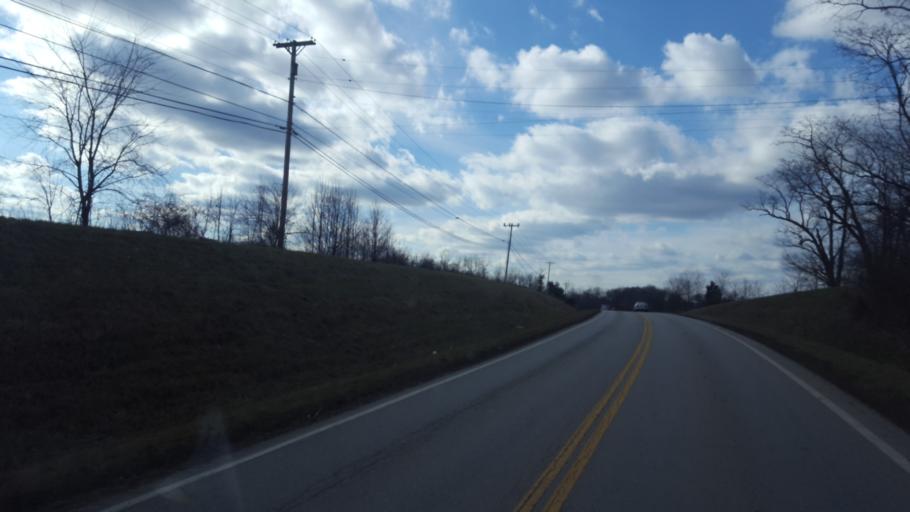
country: US
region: Kentucky
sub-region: Scott County
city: Georgetown
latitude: 38.2780
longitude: -84.5628
